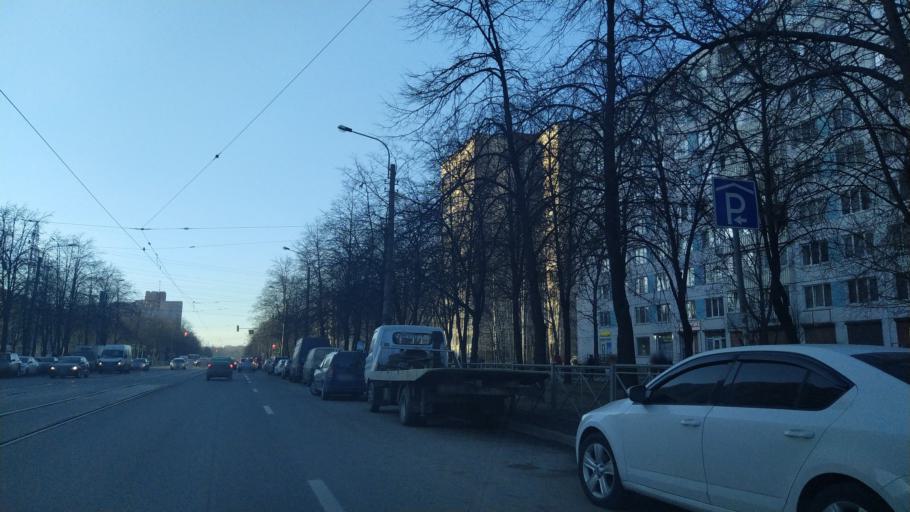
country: RU
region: Leningrad
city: Akademicheskoe
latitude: 60.0152
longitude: 30.3882
